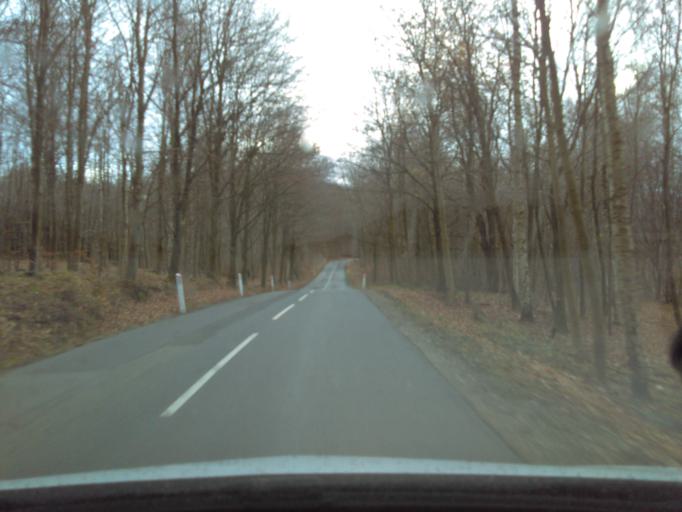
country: DK
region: Capital Region
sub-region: Fureso Kommune
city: Vaerlose
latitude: 55.7660
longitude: 12.3845
